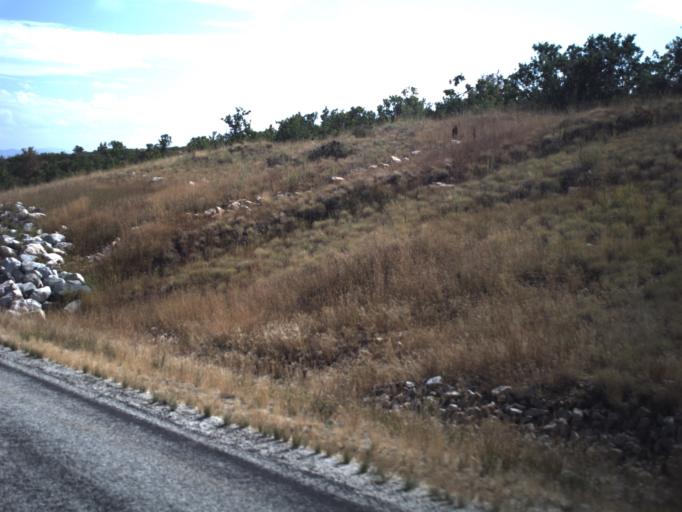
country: US
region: Utah
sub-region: Morgan County
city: Mountain Green
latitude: 41.2101
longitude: -111.8424
